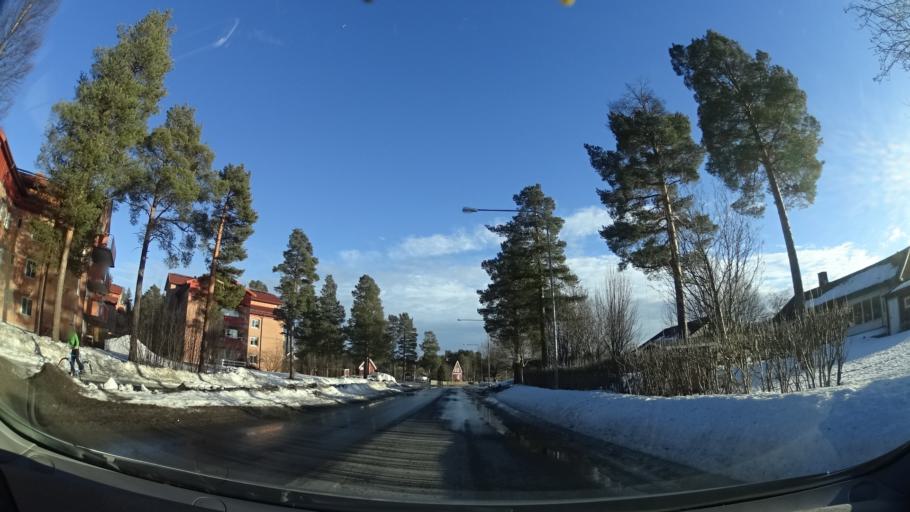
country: SE
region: Vaesterbotten
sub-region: Skelleftea Kommun
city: Byske
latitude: 64.9526
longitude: 21.2155
